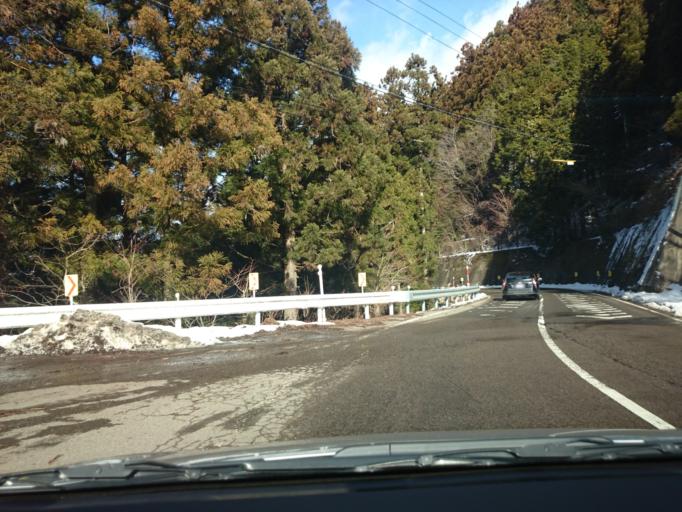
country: JP
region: Gifu
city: Gujo
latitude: 35.7353
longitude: 136.9872
